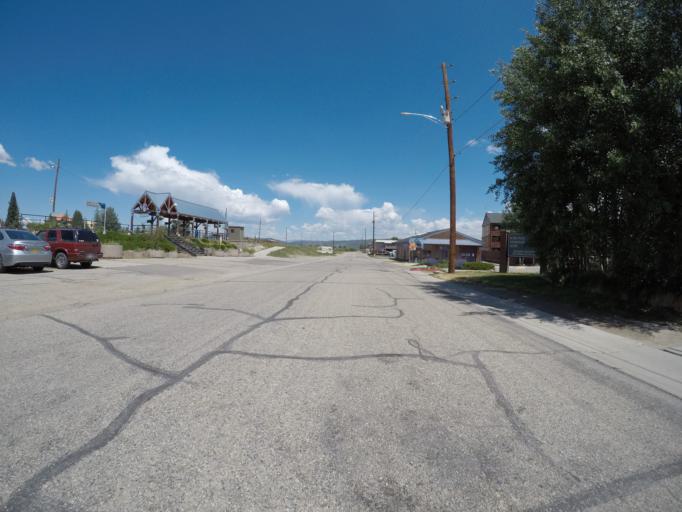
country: US
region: Colorado
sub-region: Grand County
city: Fraser
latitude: 39.9473
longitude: -105.8172
